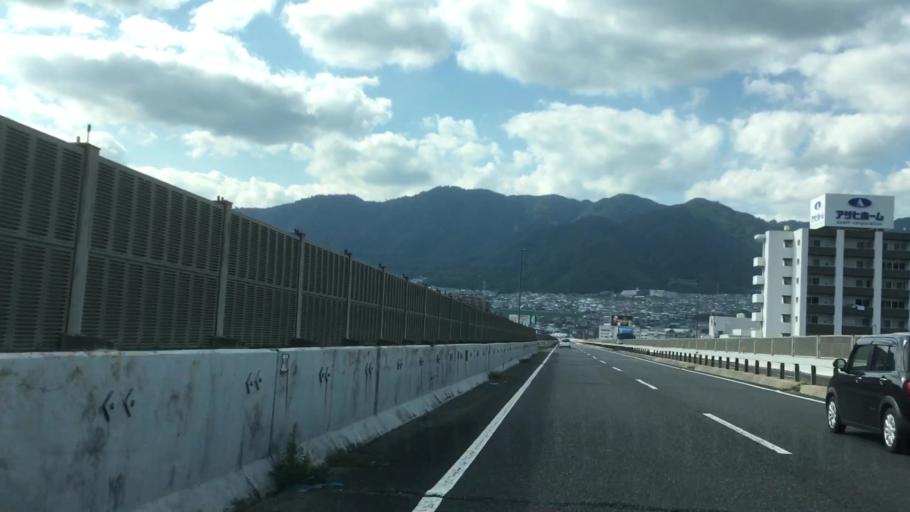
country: JP
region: Hiroshima
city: Hatsukaichi
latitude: 34.3800
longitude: 132.3613
